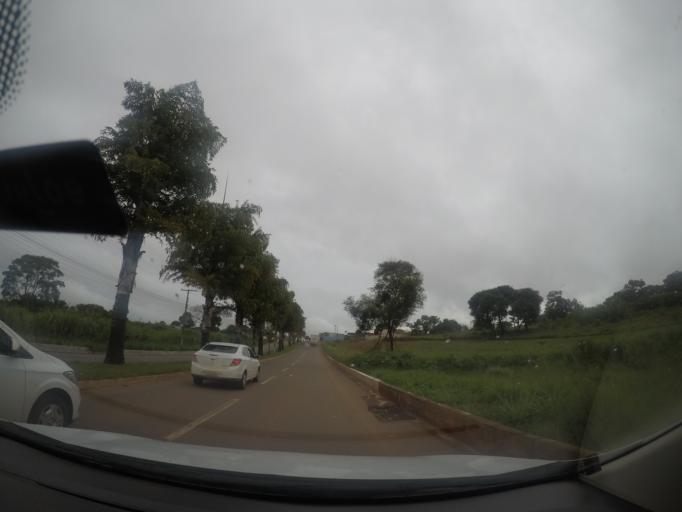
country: BR
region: Goias
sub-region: Aparecida De Goiania
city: Aparecida de Goiania
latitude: -16.7605
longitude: -49.3226
